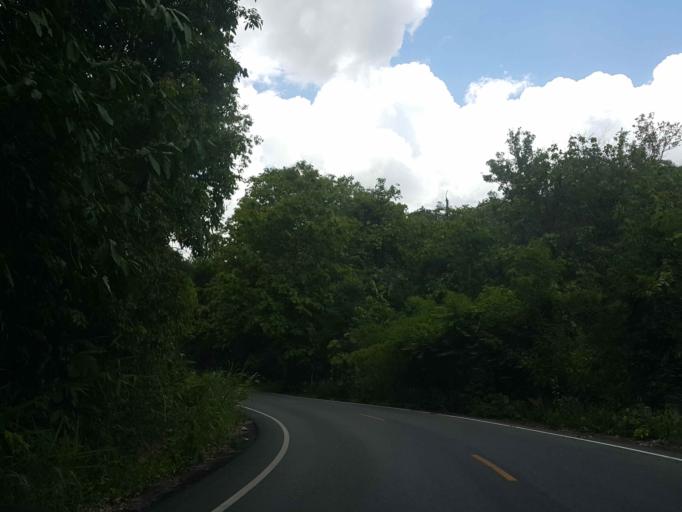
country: TH
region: Nan
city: Wiang Sa
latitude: 18.5328
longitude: 100.5532
